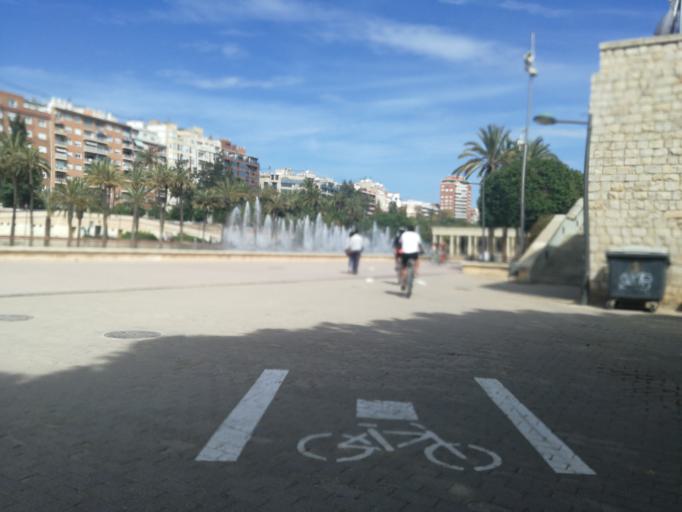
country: ES
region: Valencia
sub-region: Provincia de Valencia
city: Valencia
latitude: 39.4660
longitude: -0.3604
